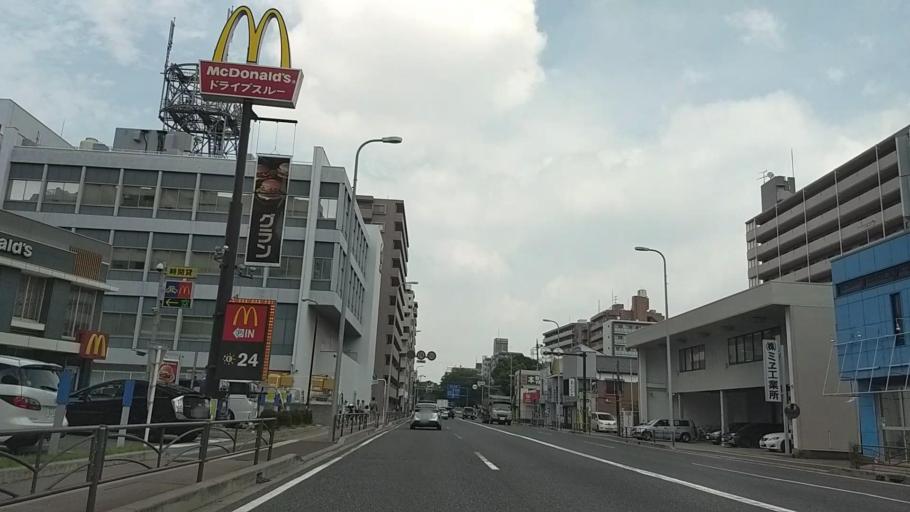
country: JP
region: Kanagawa
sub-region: Kawasaki-shi
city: Kawasaki
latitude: 35.5038
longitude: 139.6775
